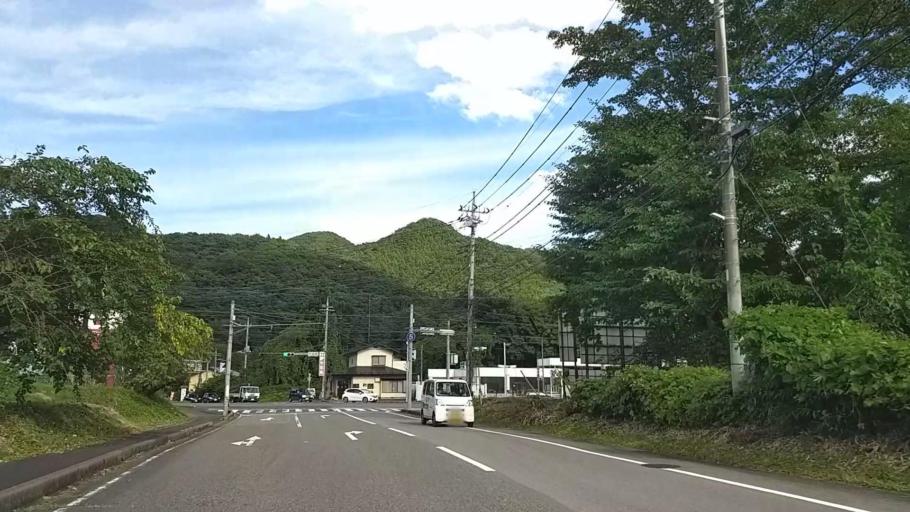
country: JP
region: Tochigi
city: Imaichi
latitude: 36.7945
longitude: 139.7005
